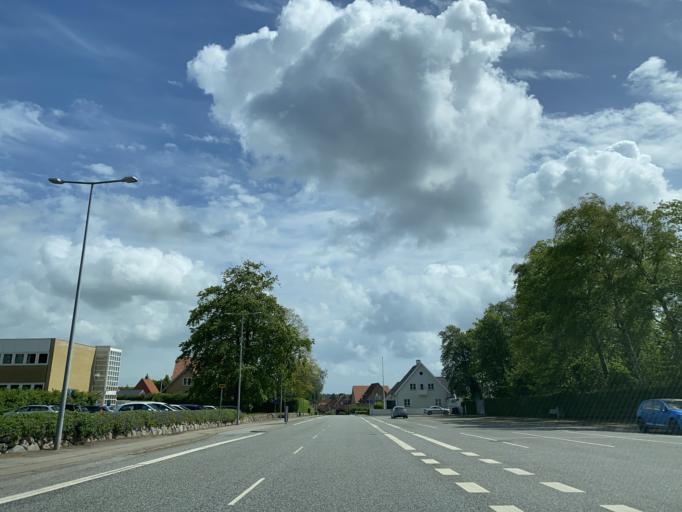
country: DK
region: South Denmark
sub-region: Sonderborg Kommune
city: Sonderborg
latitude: 54.9061
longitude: 9.7990
